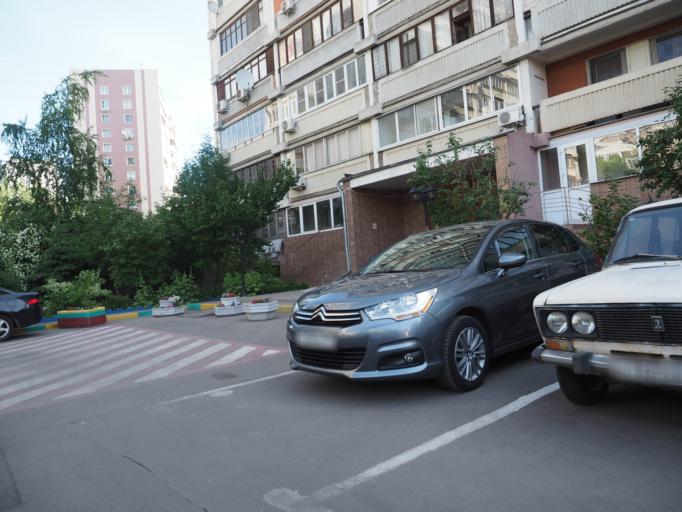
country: RU
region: Moscow
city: Lefortovo
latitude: 55.7783
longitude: 37.7266
